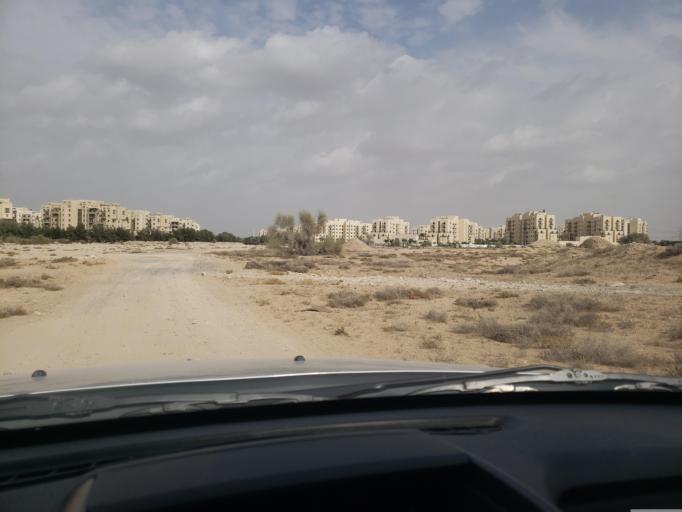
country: AE
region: Dubai
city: Dubai
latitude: 24.9999
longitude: 55.2458
